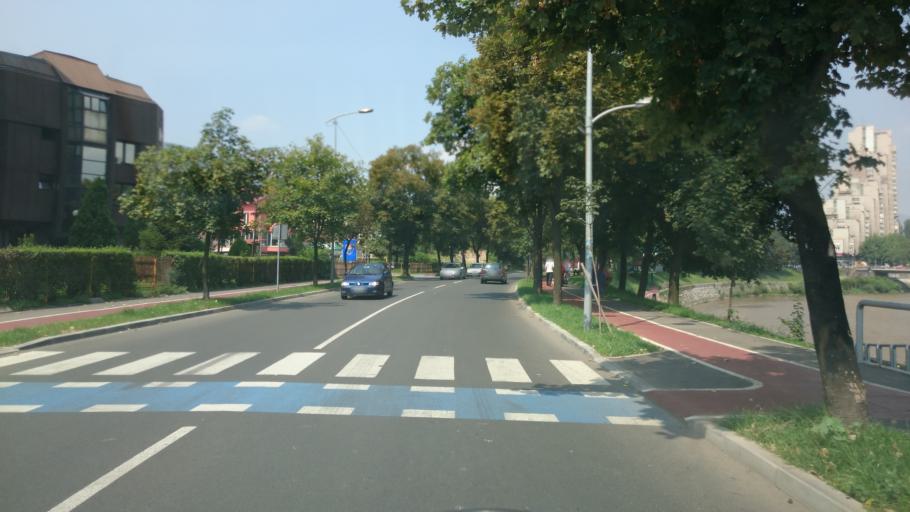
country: BA
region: Federation of Bosnia and Herzegovina
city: Zenica
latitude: 44.2004
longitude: 17.9104
